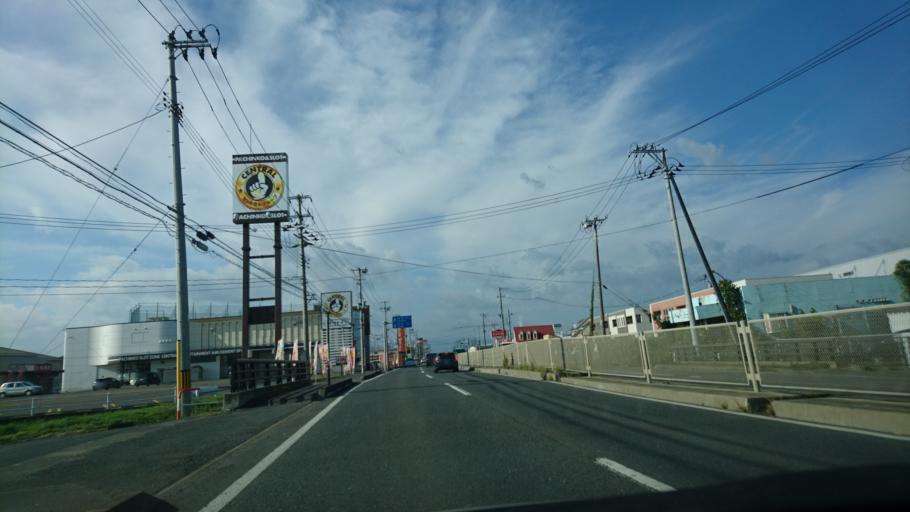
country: JP
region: Miyagi
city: Furukawa
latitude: 38.6031
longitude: 140.9786
